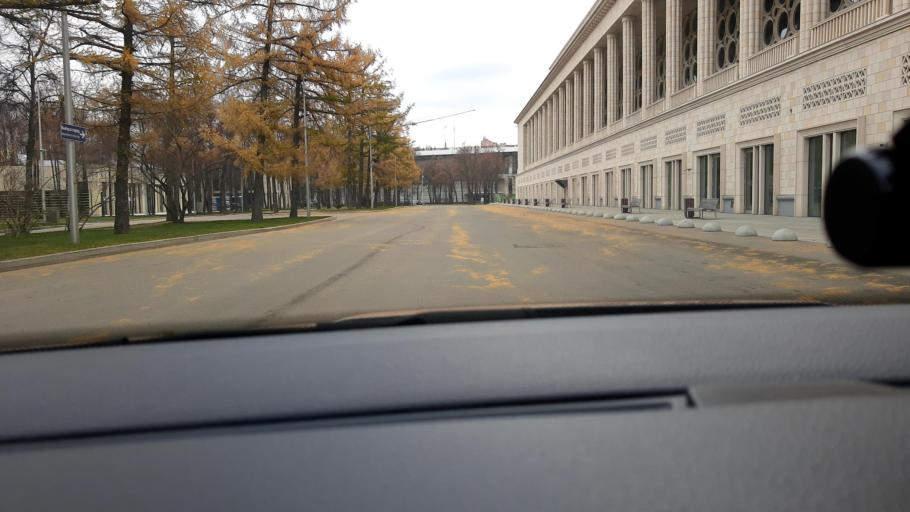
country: RU
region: Moscow
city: Luzhniki
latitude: 55.7137
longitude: 37.5585
